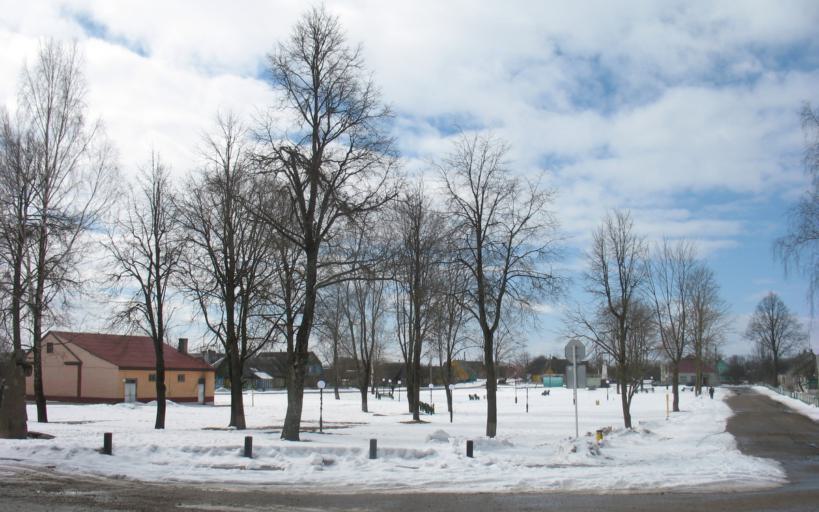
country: BY
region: Minsk
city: Narach
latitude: 55.0603
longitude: 26.6045
